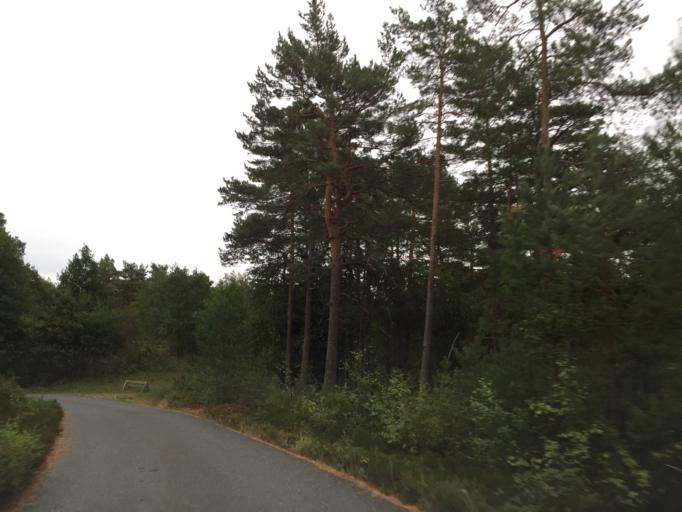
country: NO
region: Ostfold
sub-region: Hvaler
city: Skjaerhalden
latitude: 59.0806
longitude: 11.0014
